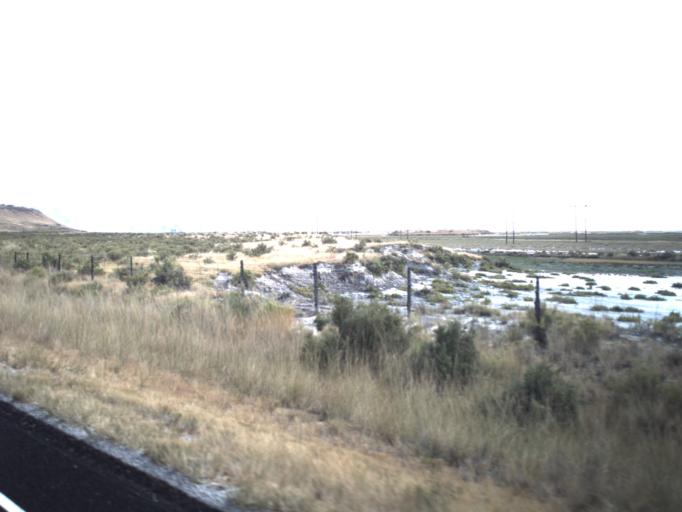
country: US
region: Utah
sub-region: Box Elder County
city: Tremonton
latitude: 41.6273
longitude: -112.4010
